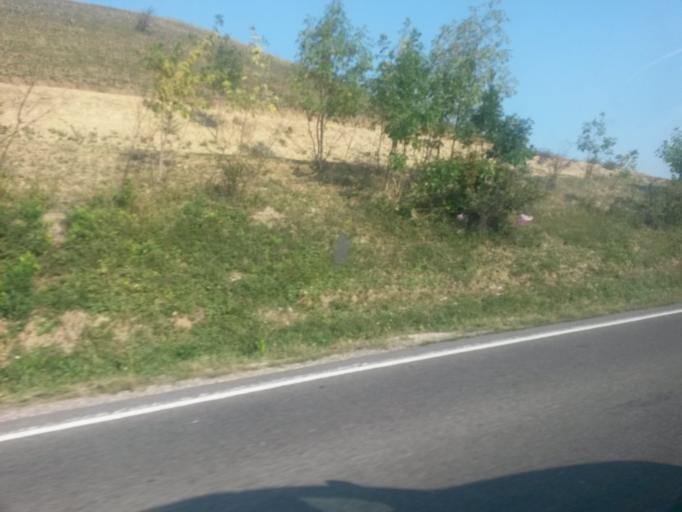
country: RO
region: Alba
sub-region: Comuna Unirea
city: Unirea
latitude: 46.4209
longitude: 23.8031
